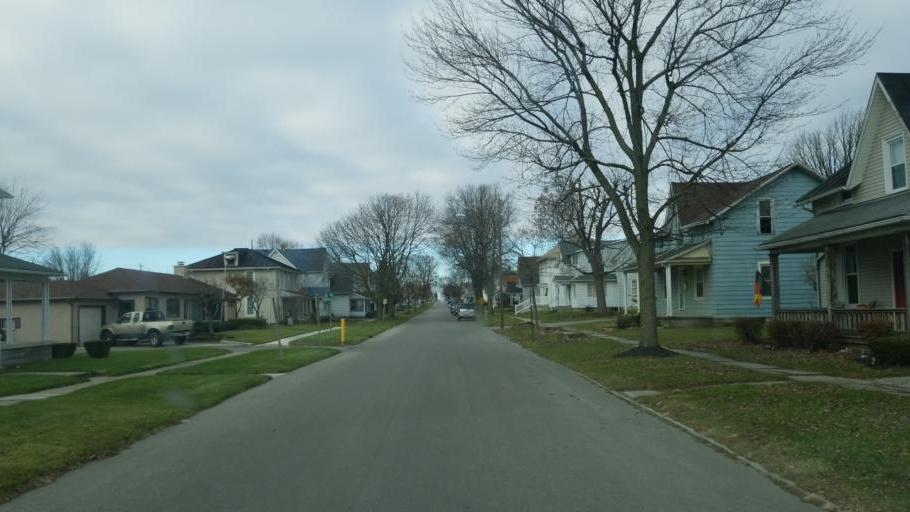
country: US
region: Ohio
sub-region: Hardin County
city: Kenton
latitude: 40.6491
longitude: -83.6015
